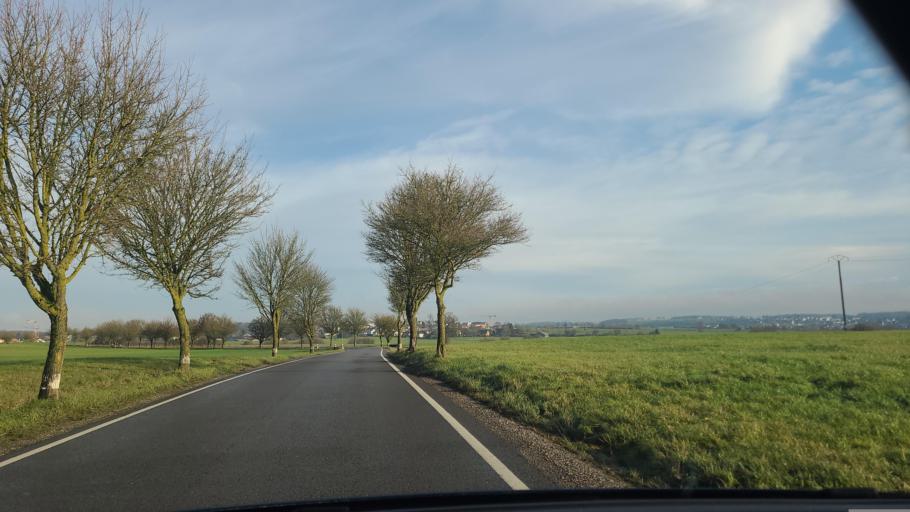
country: LU
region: Luxembourg
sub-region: Canton de Luxembourg
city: Olm
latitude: 49.6660
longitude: 5.9994
